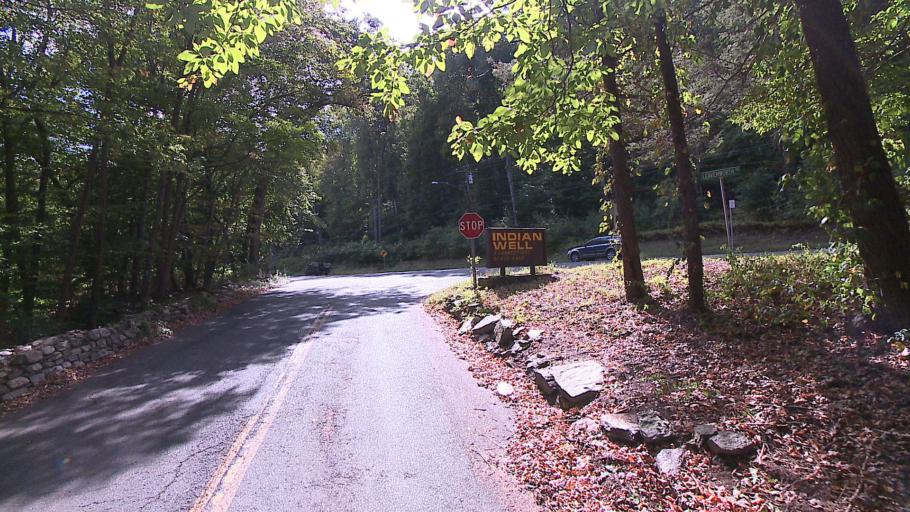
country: US
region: Connecticut
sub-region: Fairfield County
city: Shelton
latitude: 41.3335
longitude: -73.1211
